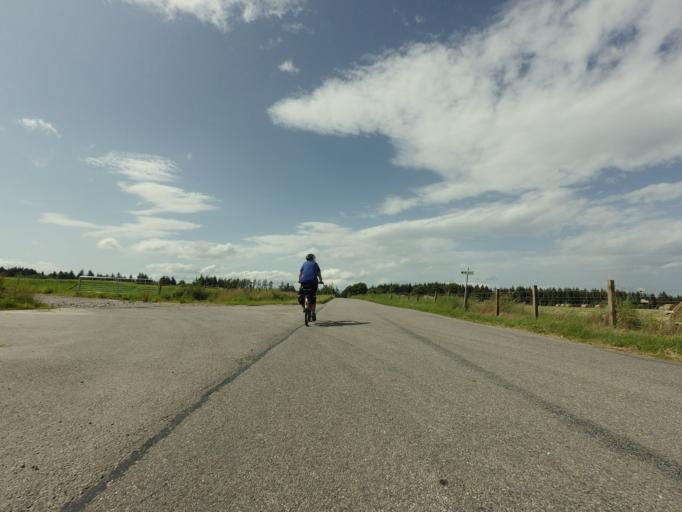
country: GB
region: Scotland
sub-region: Highland
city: Fortrose
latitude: 57.4878
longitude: -4.1013
